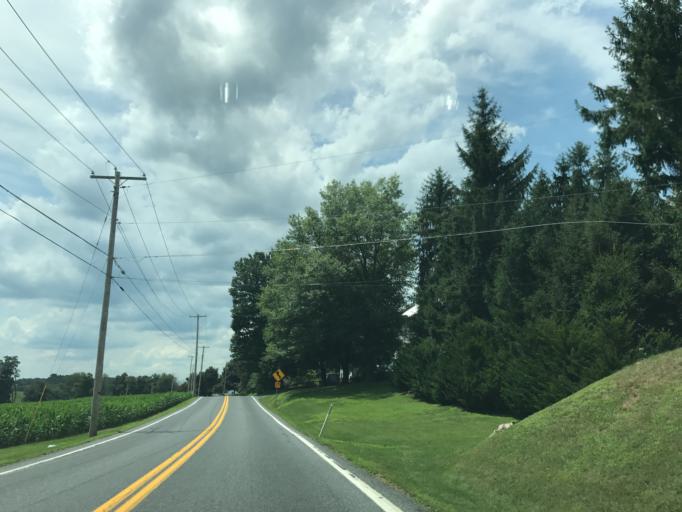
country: US
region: Pennsylvania
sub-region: Lancaster County
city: Manheim
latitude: 40.1994
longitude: -76.4418
